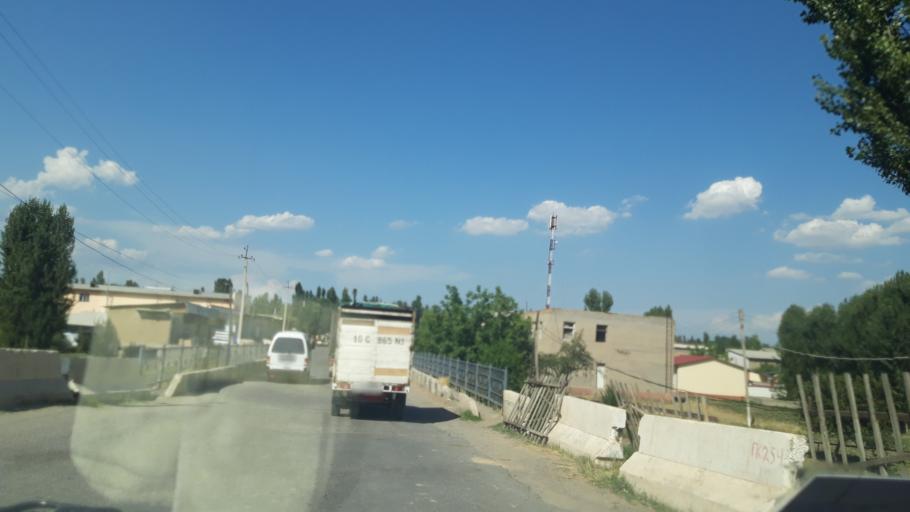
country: UZ
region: Namangan
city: Yangiqo`rg`on
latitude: 41.2074
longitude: 71.7042
